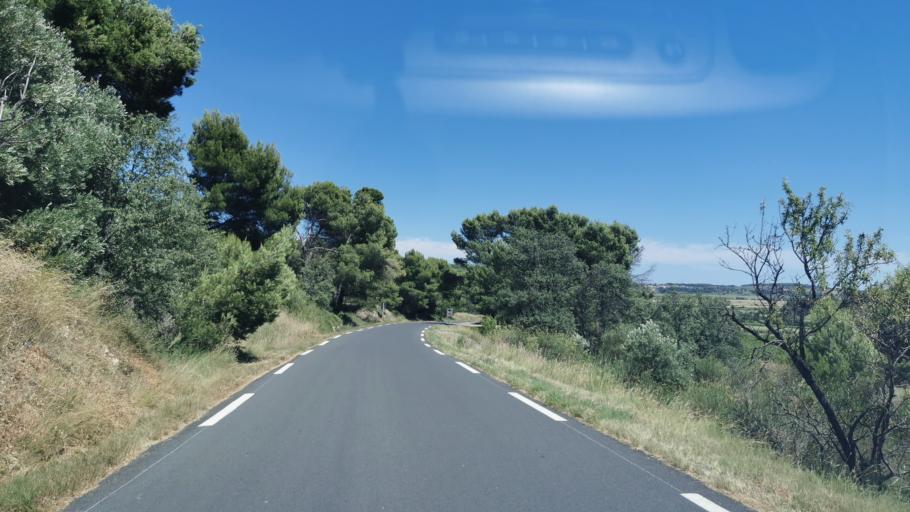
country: FR
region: Languedoc-Roussillon
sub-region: Departement de l'Herault
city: Nissan-lez-Enserune
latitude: 43.2770
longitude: 3.1200
